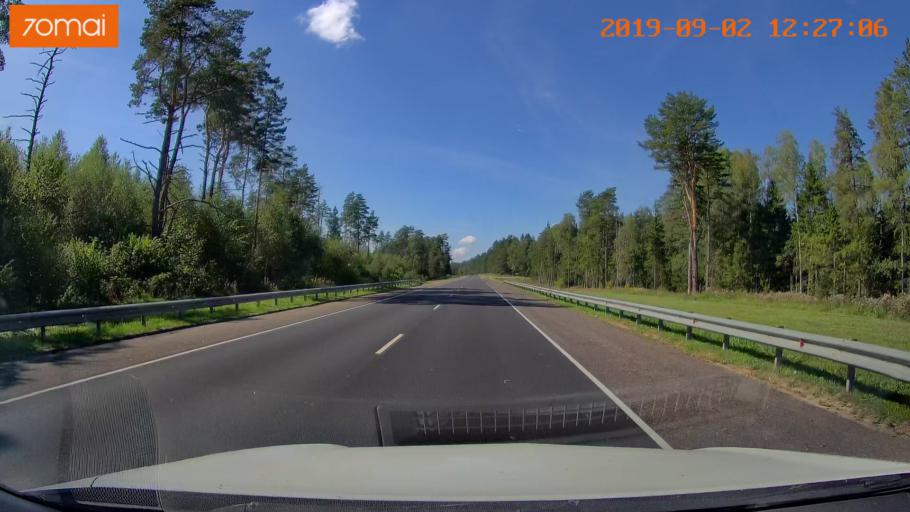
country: RU
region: Smolensk
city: Shumyachi
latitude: 53.8546
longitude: 32.5530
